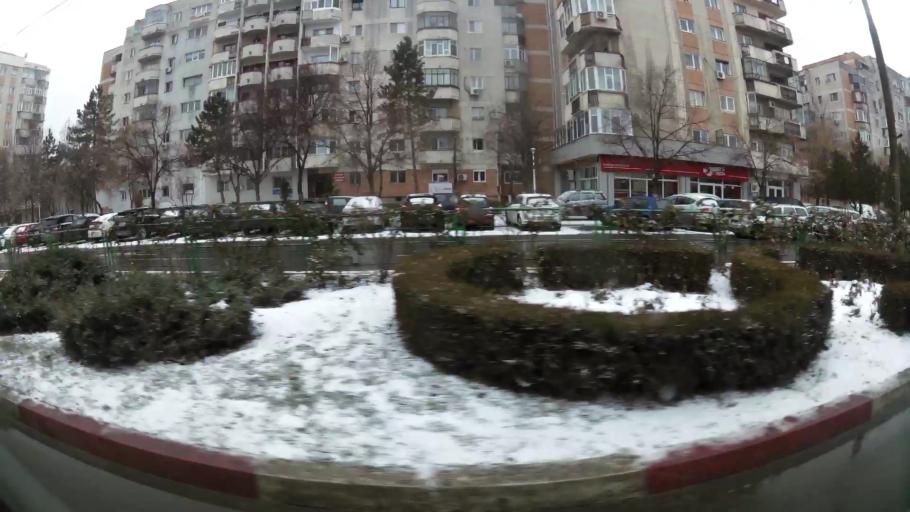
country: RO
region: Prahova
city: Ploiesti
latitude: 44.9454
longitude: 26.0139
